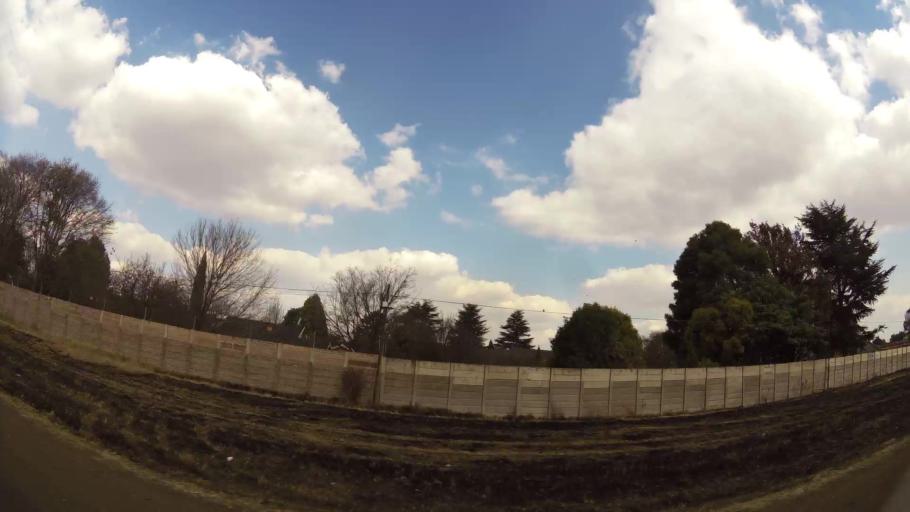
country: ZA
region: Mpumalanga
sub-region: Nkangala District Municipality
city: Delmas
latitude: -26.1402
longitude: 28.6691
